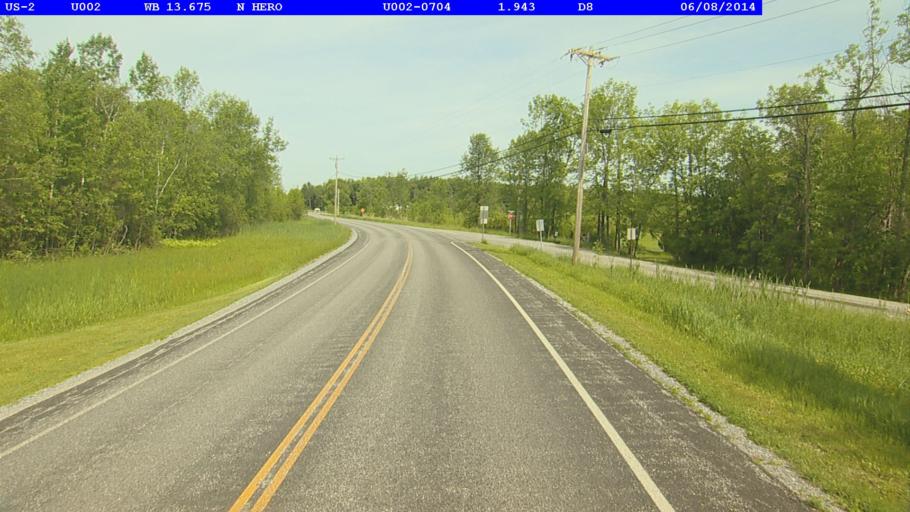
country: US
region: Vermont
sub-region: Grand Isle County
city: North Hero
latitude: 44.8619
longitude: -73.2598
